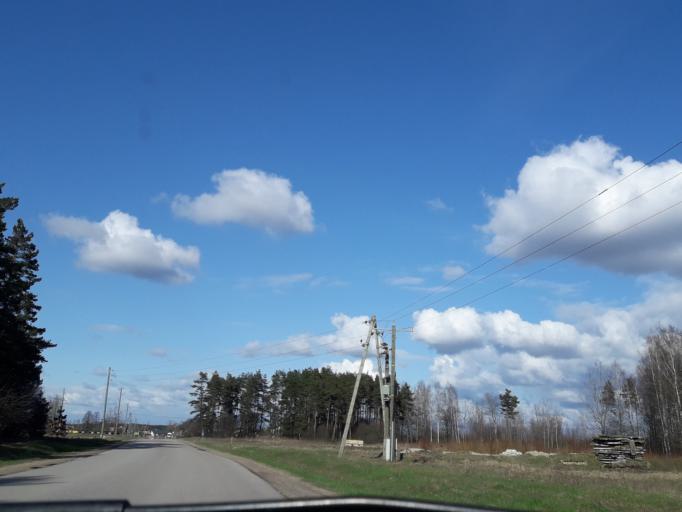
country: LV
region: Kekava
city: Kekava
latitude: 56.8339
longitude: 24.2043
